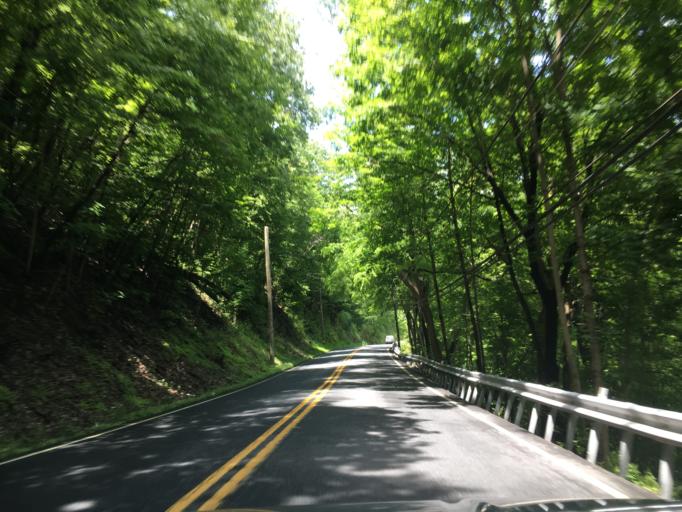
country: US
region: Pennsylvania
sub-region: Lehigh County
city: Cementon
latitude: 40.6956
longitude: -75.5125
